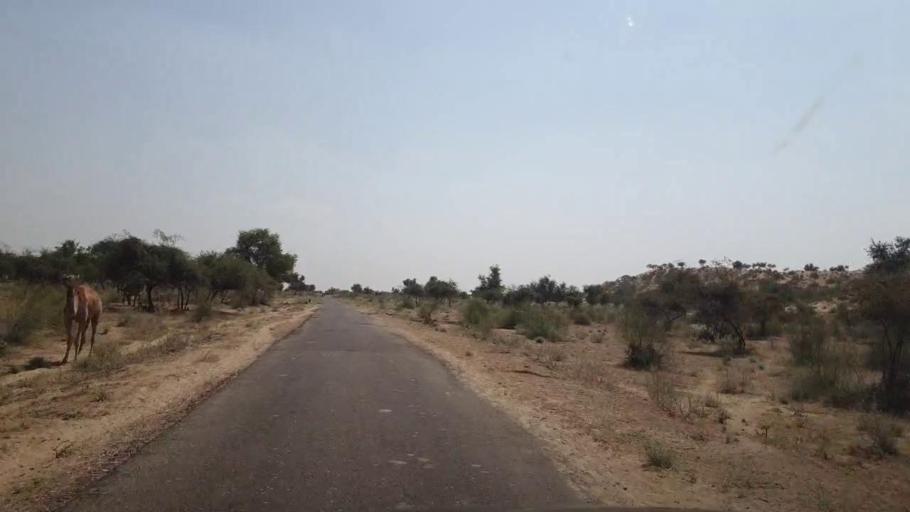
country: PK
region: Sindh
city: Islamkot
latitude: 25.1026
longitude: 70.7244
